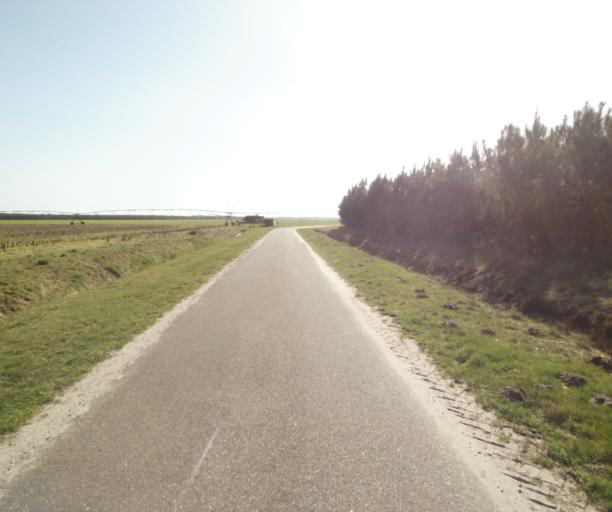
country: FR
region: Aquitaine
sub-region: Departement des Landes
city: Roquefort
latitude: 44.1753
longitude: -0.2509
